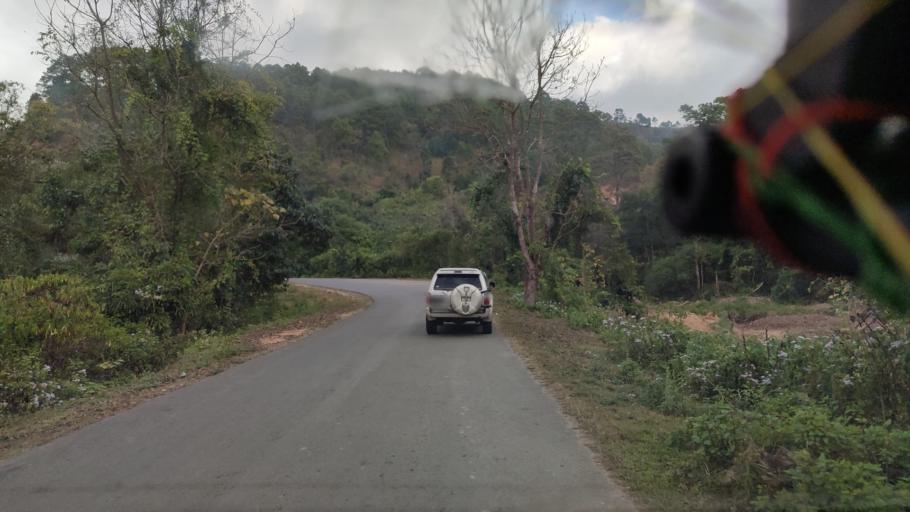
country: MM
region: Shan
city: Taunggyi
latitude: 21.1658
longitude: 97.6022
